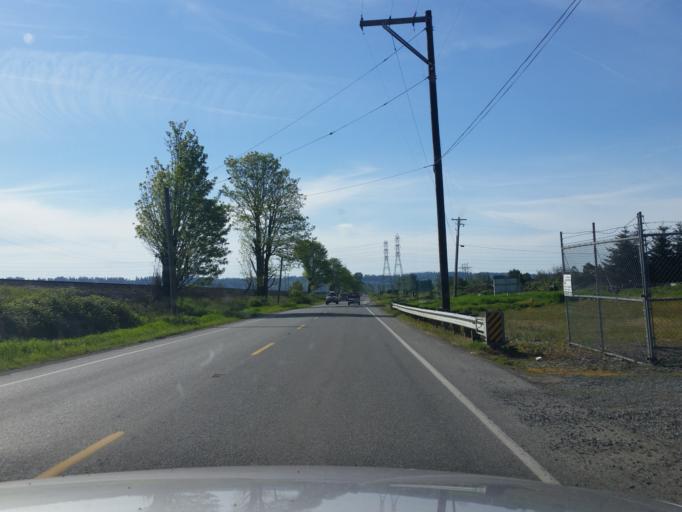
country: US
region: Washington
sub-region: Snohomish County
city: Snohomish
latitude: 47.9156
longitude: -122.1298
